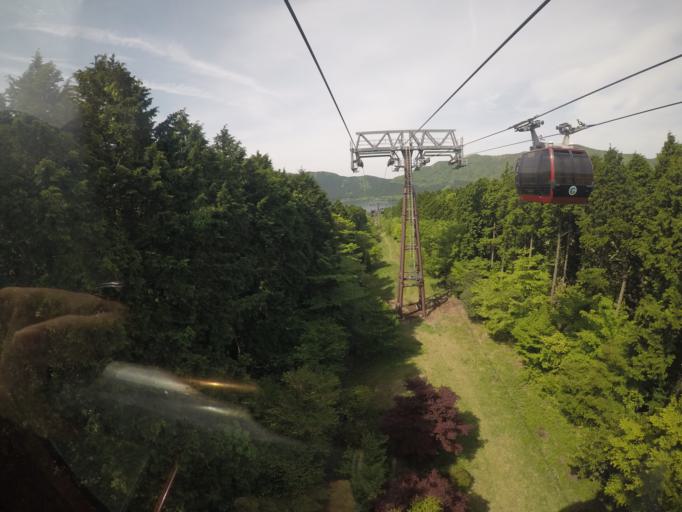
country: JP
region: Kanagawa
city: Hakone
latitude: 35.2409
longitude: 138.9997
